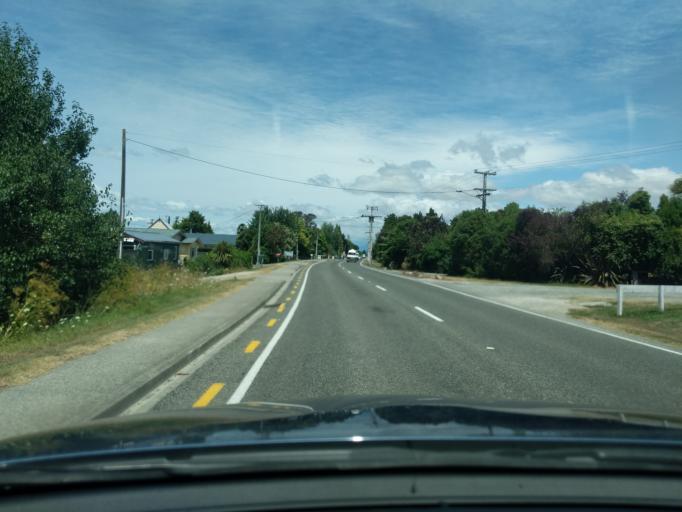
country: NZ
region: Tasman
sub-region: Tasman District
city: Motueka
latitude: -41.0817
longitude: 172.9971
